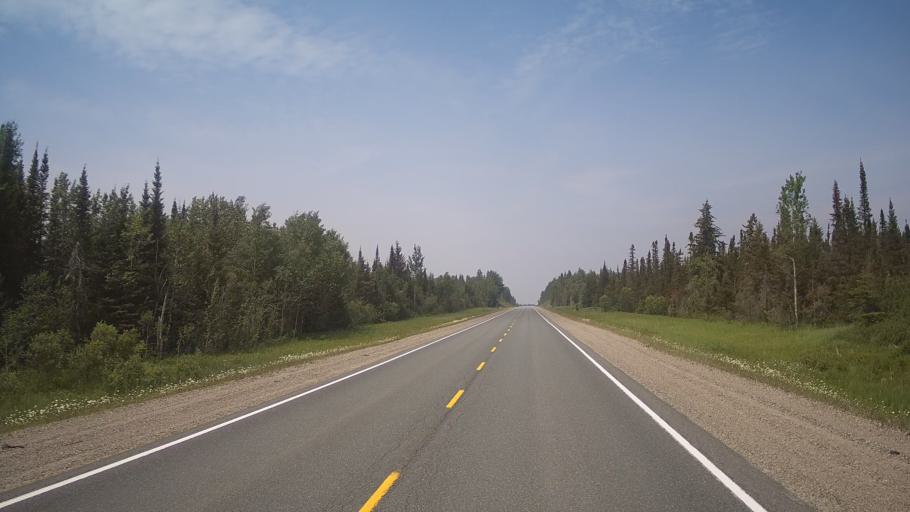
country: CA
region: Ontario
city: Timmins
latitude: 48.7440
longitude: -81.3569
